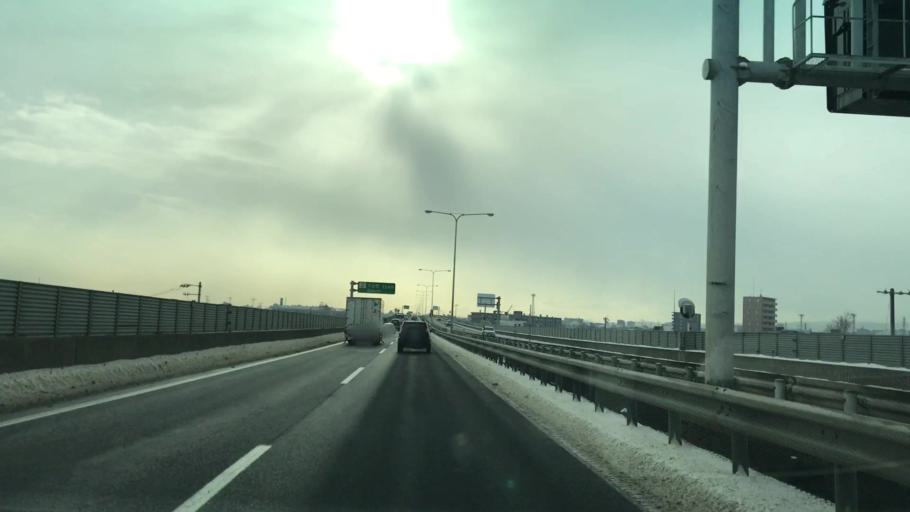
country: JP
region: Hokkaido
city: Sapporo
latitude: 43.0554
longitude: 141.4280
